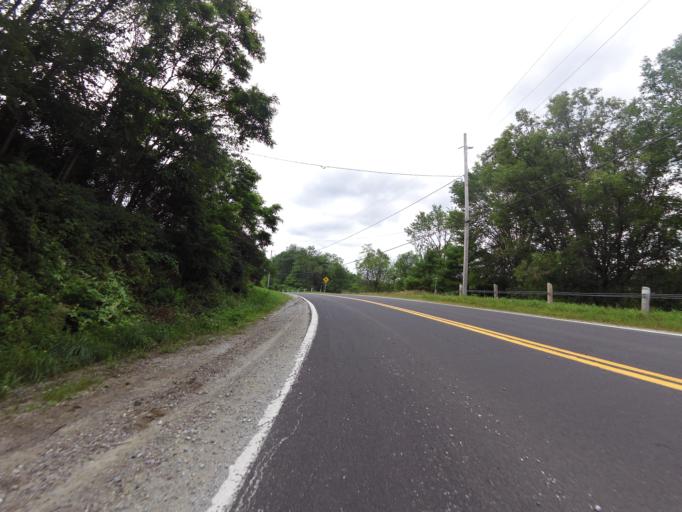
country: CA
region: Ontario
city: Perth
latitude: 44.8371
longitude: -76.5342
